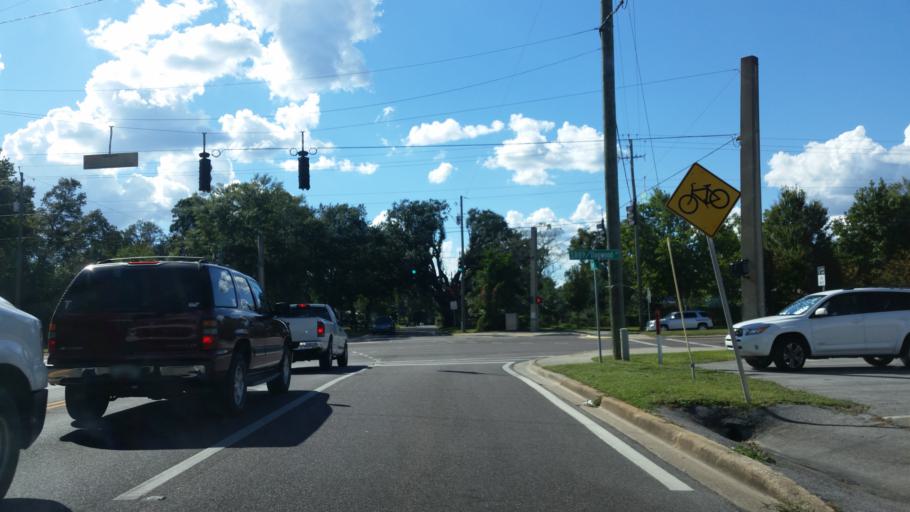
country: US
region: Florida
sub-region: Santa Rosa County
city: Milton
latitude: 30.6310
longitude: -87.0552
